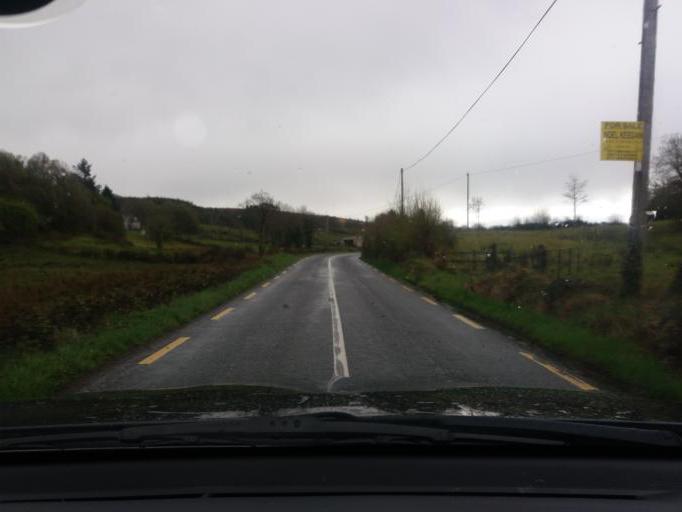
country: IE
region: Connaught
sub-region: County Leitrim
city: Manorhamilton
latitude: 54.2741
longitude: -7.9372
